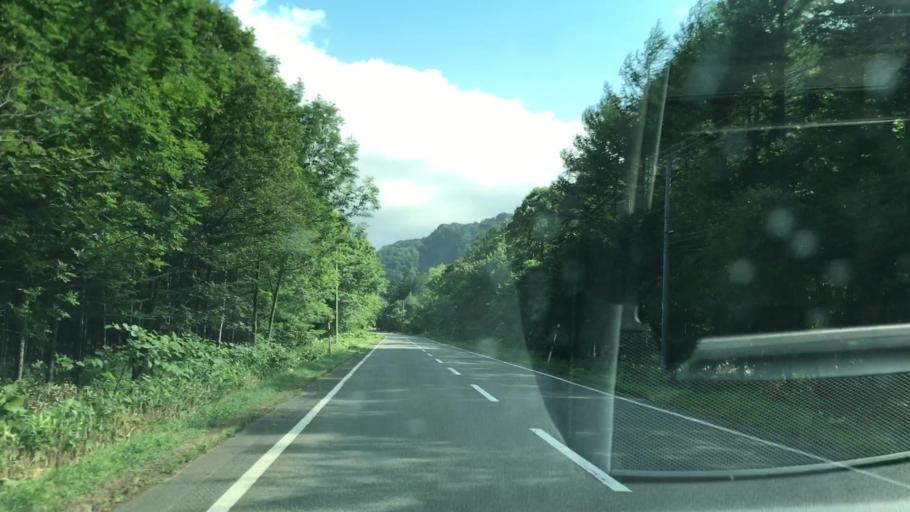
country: JP
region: Hokkaido
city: Shizunai-furukawacho
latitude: 42.8281
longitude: 142.4162
